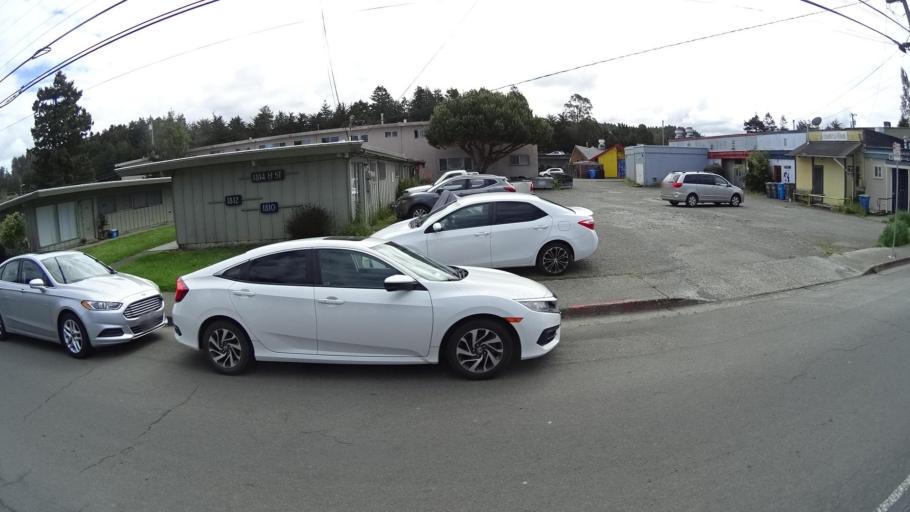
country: US
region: California
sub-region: Humboldt County
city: Arcata
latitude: 40.8766
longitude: -124.0839
